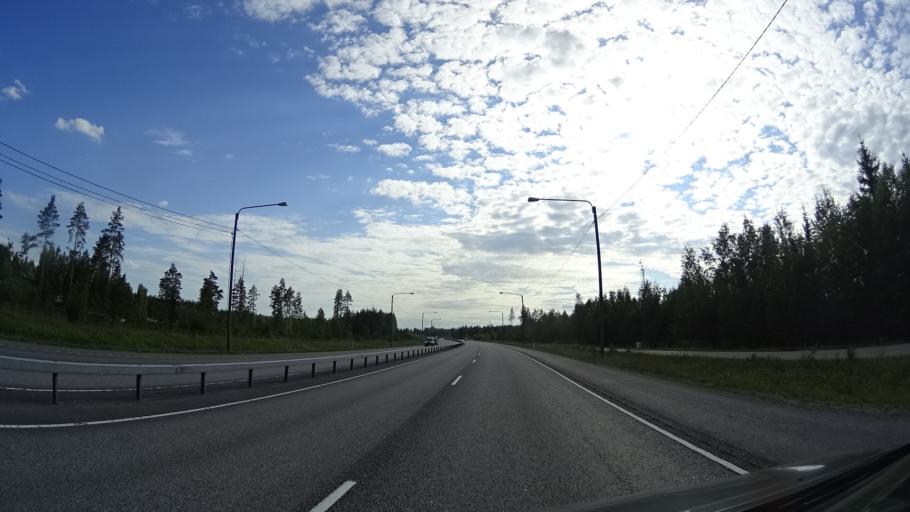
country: FI
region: South Karelia
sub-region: Lappeenranta
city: Joutseno
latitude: 61.0963
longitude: 28.3757
